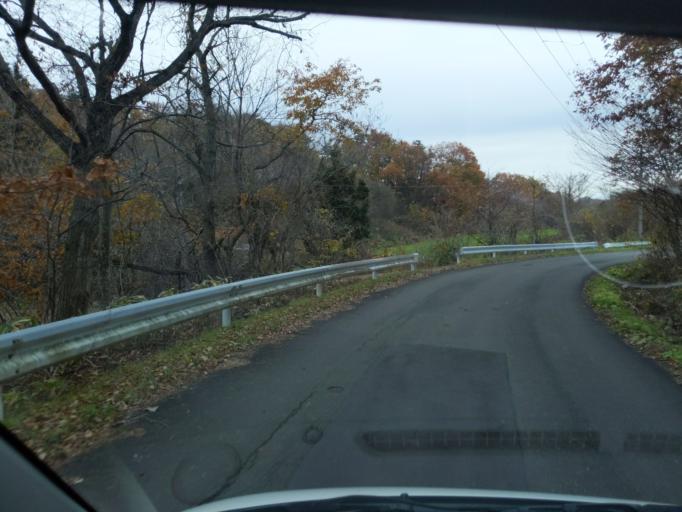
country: JP
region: Iwate
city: Ichinoseki
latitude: 38.9892
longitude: 141.0123
